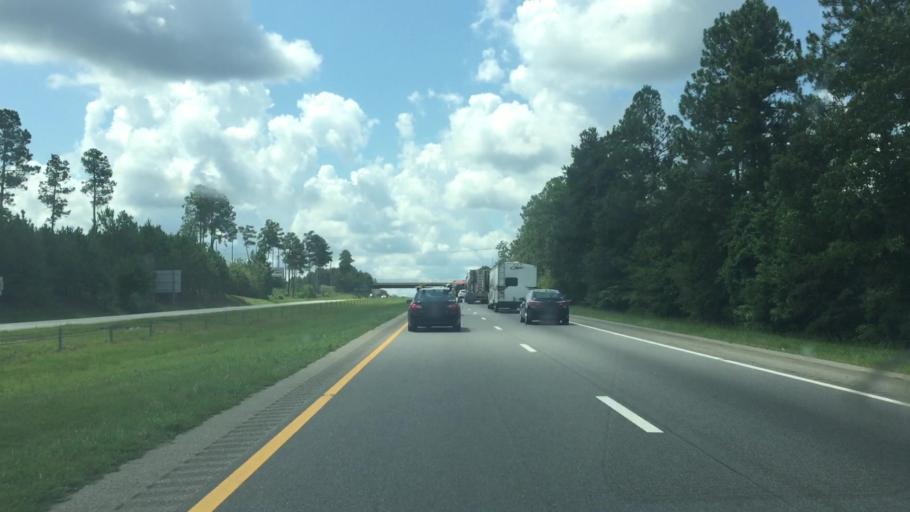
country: US
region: North Carolina
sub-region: Richmond County
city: East Rockingham
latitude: 34.9033
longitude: -79.7903
